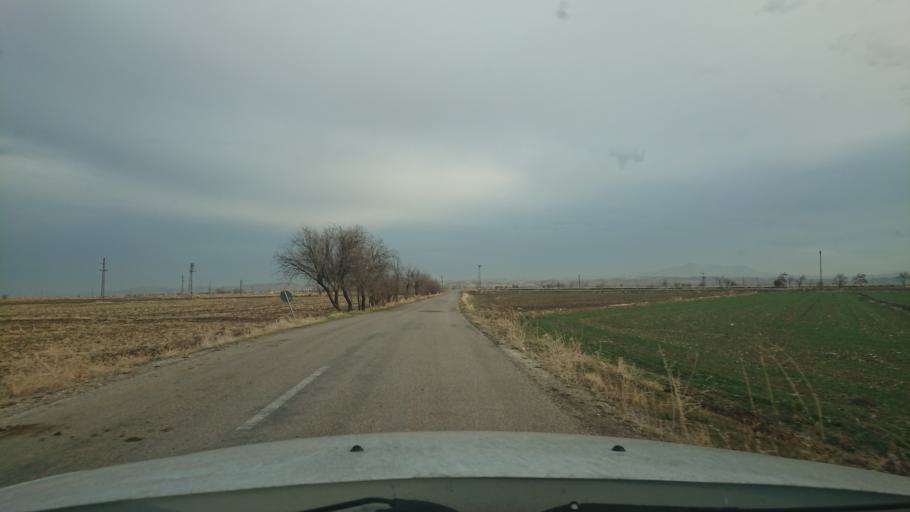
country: TR
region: Aksaray
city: Yesilova
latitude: 38.4298
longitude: 33.8355
